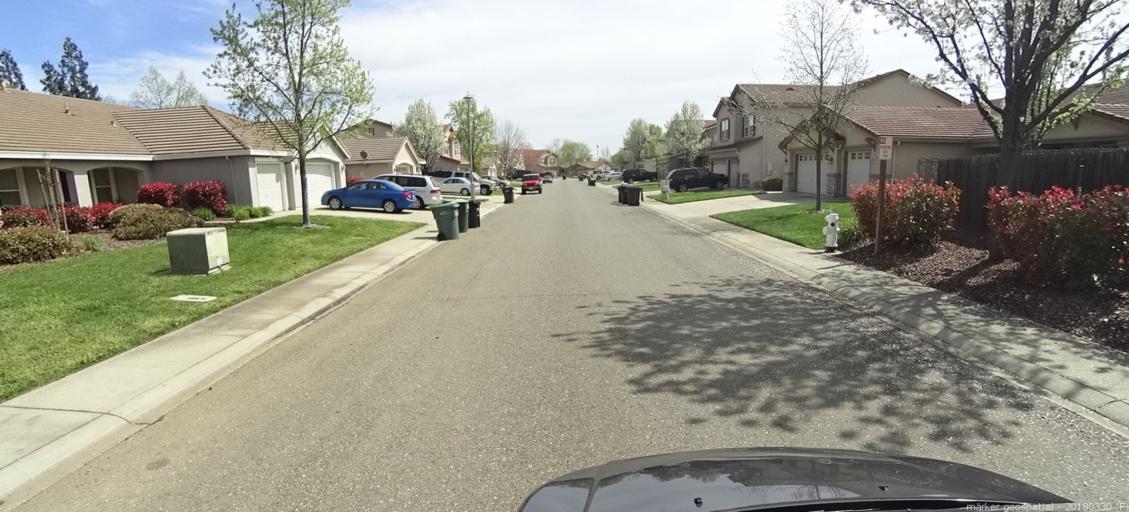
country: US
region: California
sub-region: Sacramento County
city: Rancho Cordova
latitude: 38.5429
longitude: -121.2792
